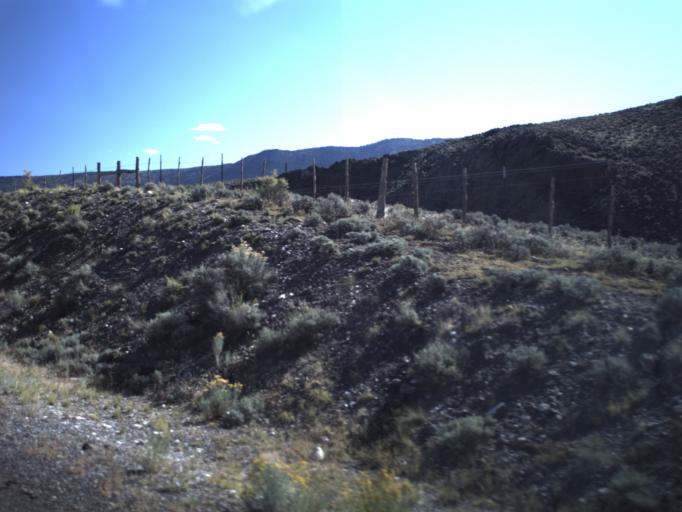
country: US
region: Utah
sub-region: Piute County
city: Junction
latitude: 38.3529
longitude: -111.9476
